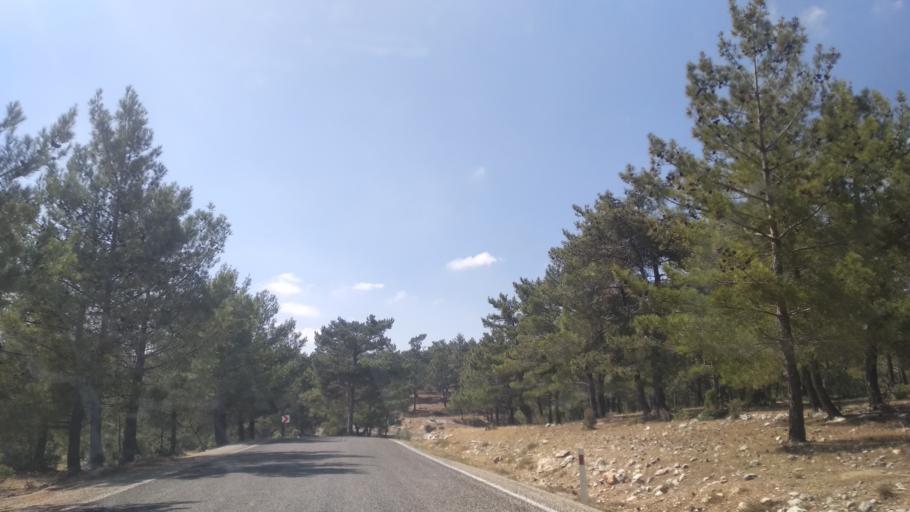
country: TR
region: Mersin
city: Gulnar
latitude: 36.3027
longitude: 33.4595
